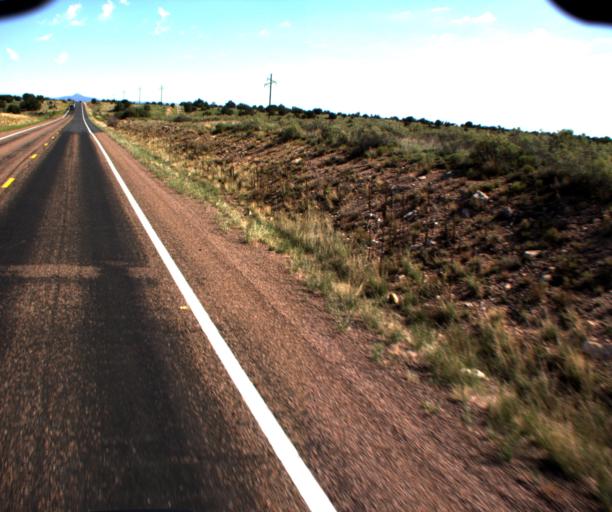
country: US
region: Arizona
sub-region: Coconino County
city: Williams
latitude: 35.5842
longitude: -112.1514
